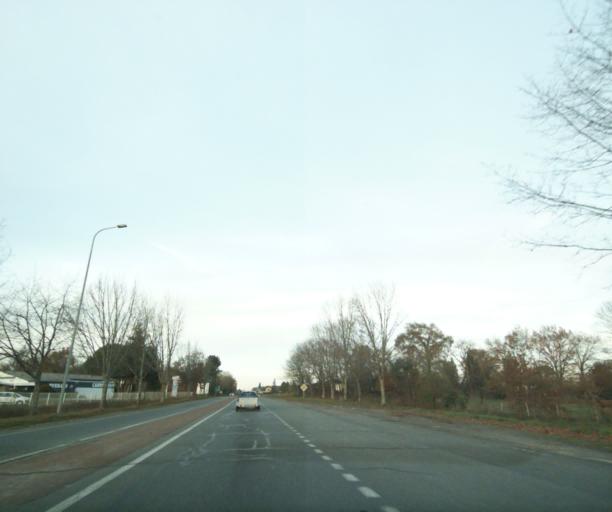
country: FR
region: Aquitaine
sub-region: Departement de la Gironde
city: Bazas
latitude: 44.4448
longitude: -0.2359
